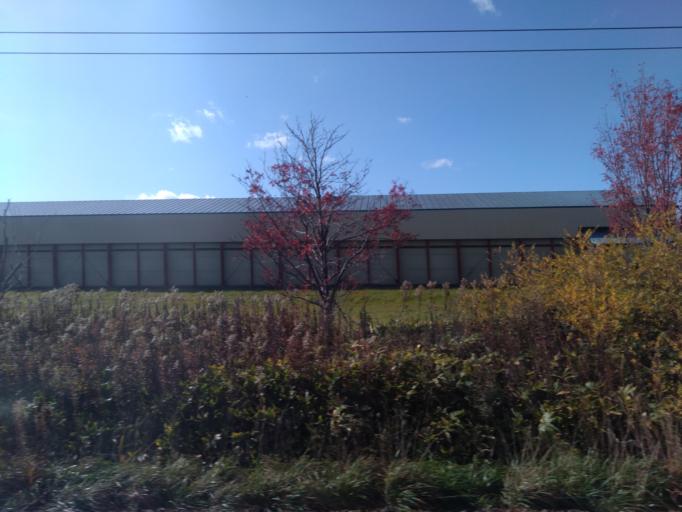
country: JP
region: Hokkaido
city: Kitahiroshima
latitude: 42.9570
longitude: 141.5695
